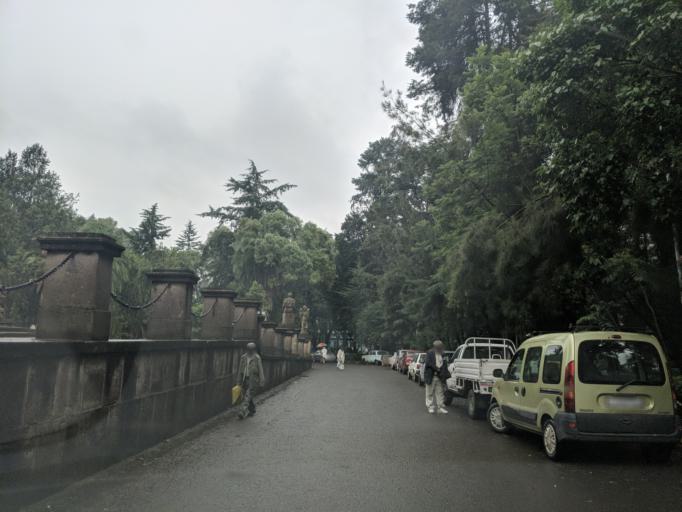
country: ET
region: Adis Abeba
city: Addis Ababa
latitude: 9.0310
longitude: 38.7665
